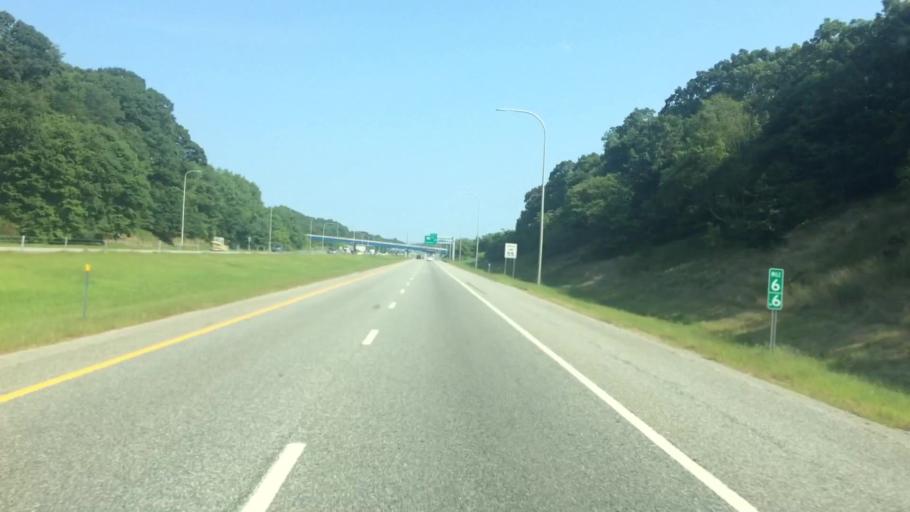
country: US
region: Rhode Island
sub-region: Kent County
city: East Greenwich
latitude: 41.6223
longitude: -71.4866
